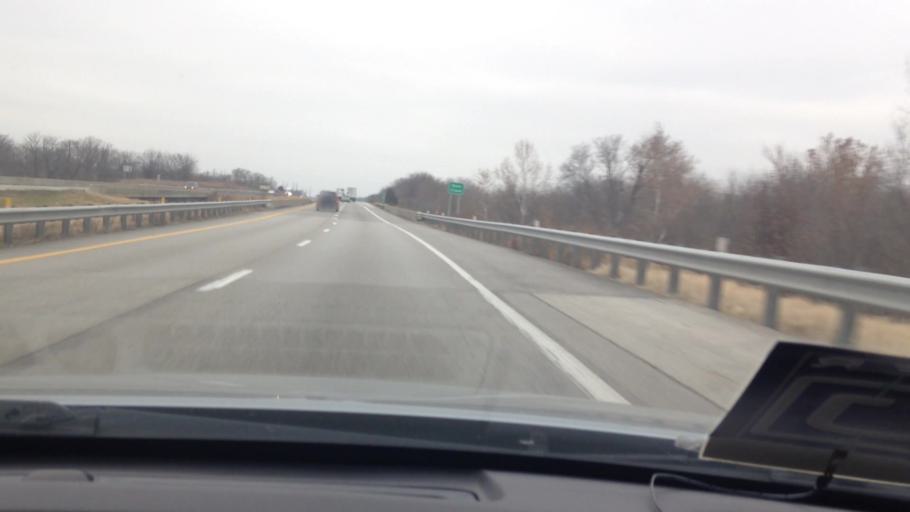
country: US
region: Missouri
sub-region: Cass County
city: Raymore
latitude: 38.7698
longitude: -94.4911
